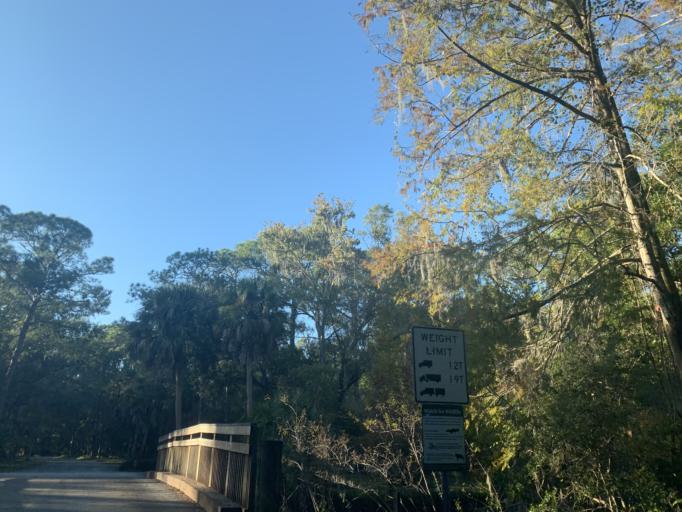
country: US
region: Florida
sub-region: Pinellas County
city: East Lake
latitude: 28.0927
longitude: -82.7064
